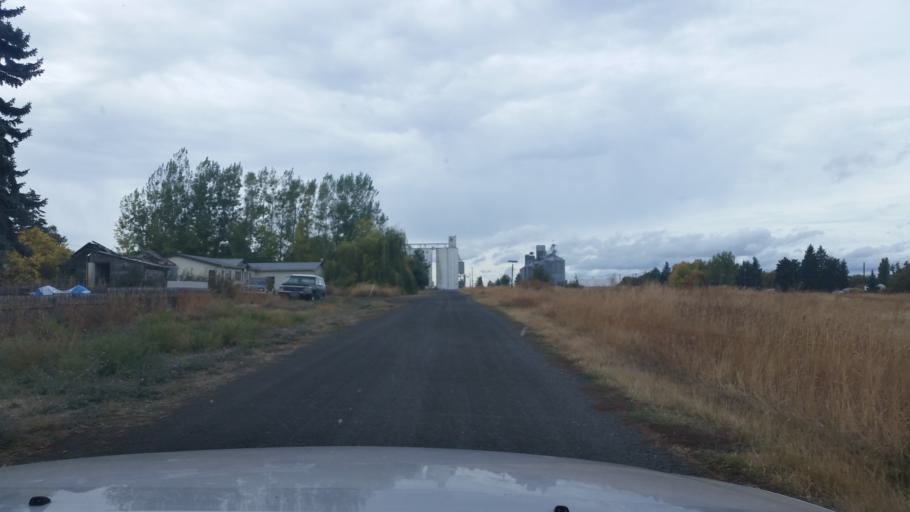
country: US
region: Washington
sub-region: Spokane County
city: Medical Lake
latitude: 47.6706
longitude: -117.8725
